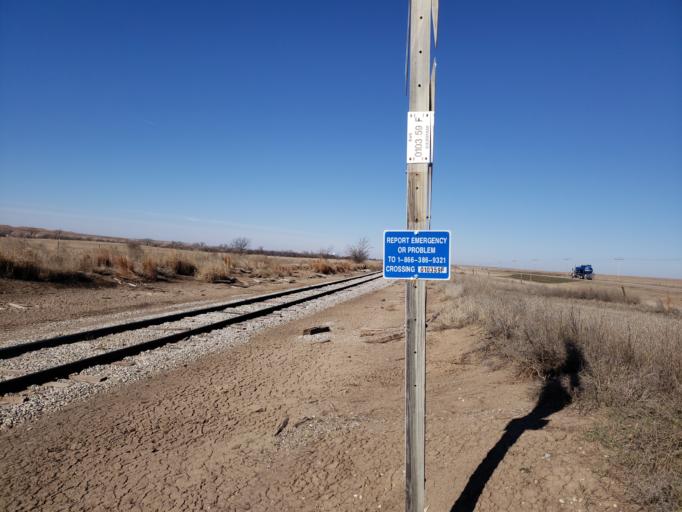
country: US
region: Kansas
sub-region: Ness County
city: Ness City
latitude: 38.4500
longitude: -100.1396
